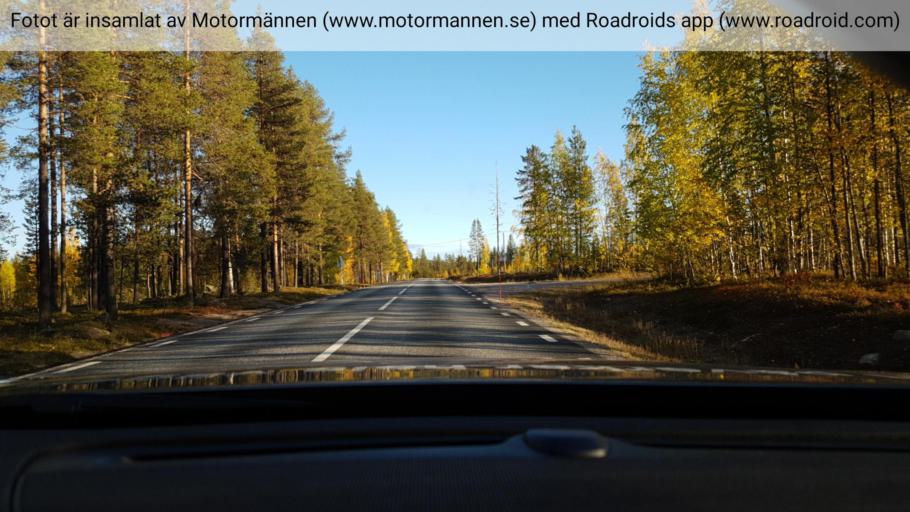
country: SE
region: Norrbotten
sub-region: Jokkmokks Kommun
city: Jokkmokk
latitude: 66.7985
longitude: 19.8759
